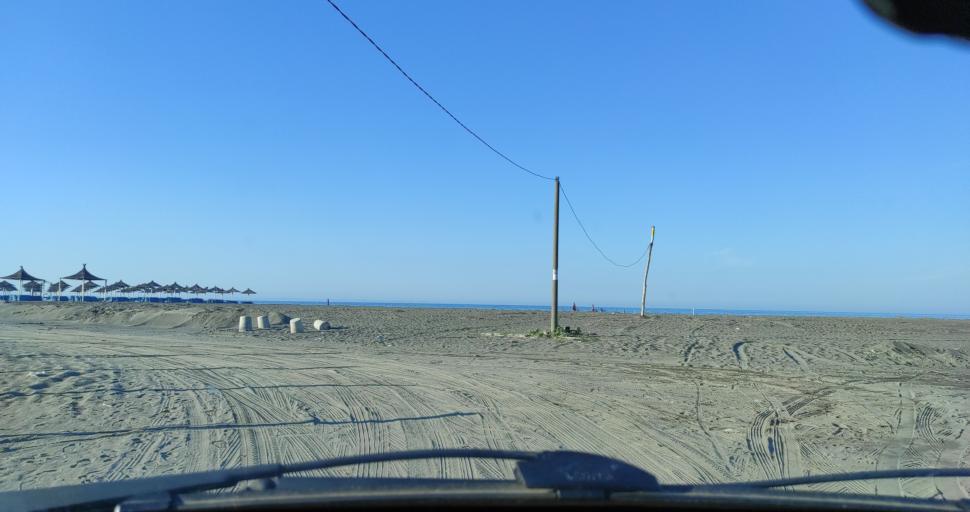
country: AL
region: Shkoder
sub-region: Rrethi i Shkodres
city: Velipoje
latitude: 41.8607
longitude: 19.4357
